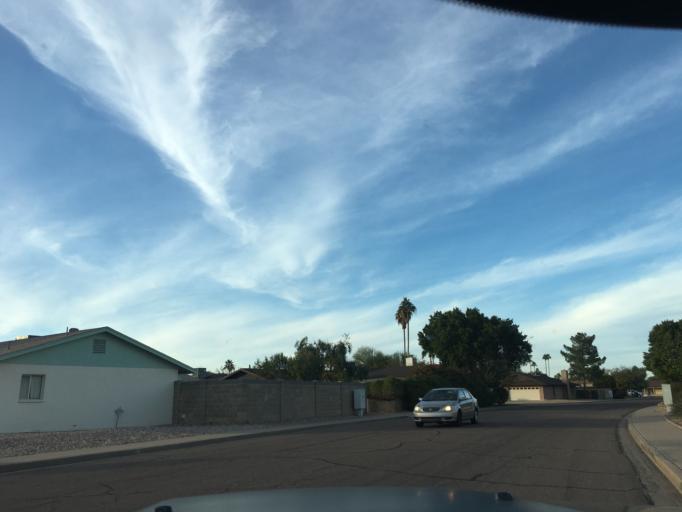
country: US
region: Arizona
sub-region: Maricopa County
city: Tempe
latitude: 33.3733
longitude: -111.9079
